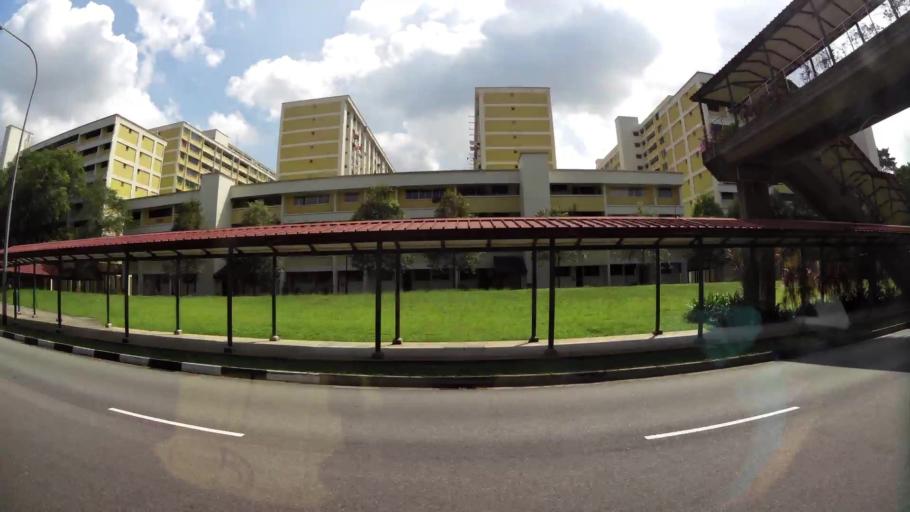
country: SG
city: Singapore
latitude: 1.3466
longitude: 103.8469
